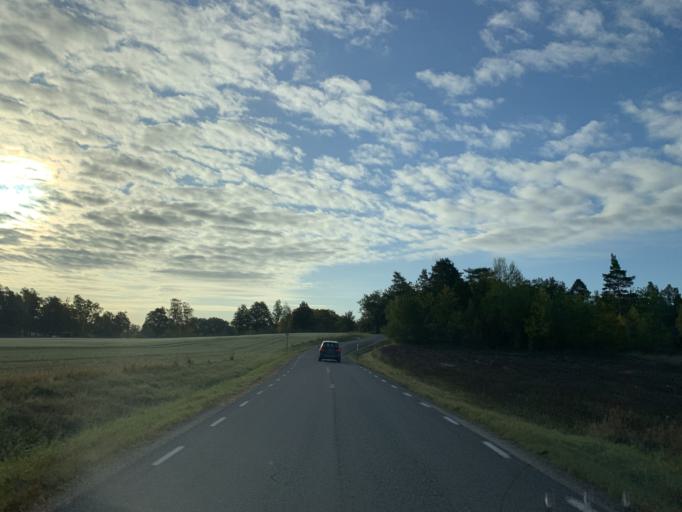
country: SE
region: Stockholm
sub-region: Upplands-Bro Kommun
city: Bro
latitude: 59.5015
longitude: 17.5883
